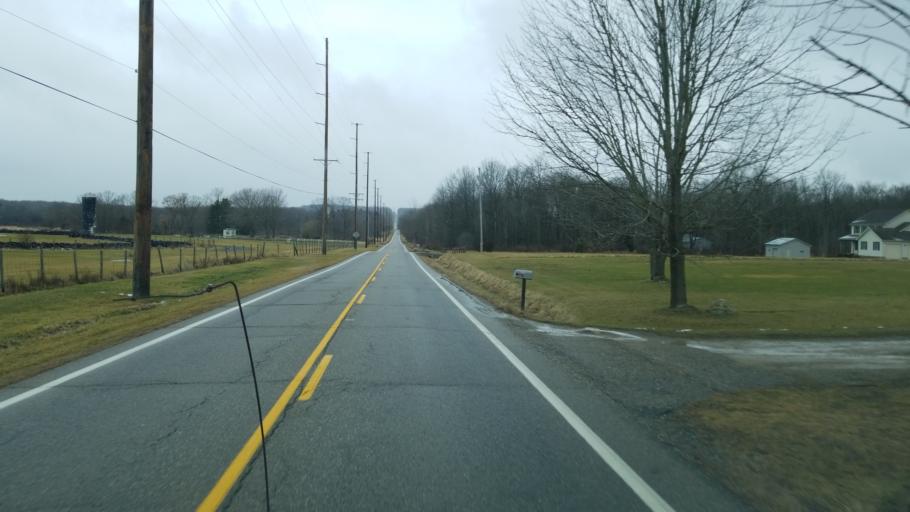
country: US
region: Ohio
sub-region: Portage County
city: Windham
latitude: 41.3101
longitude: -81.0130
